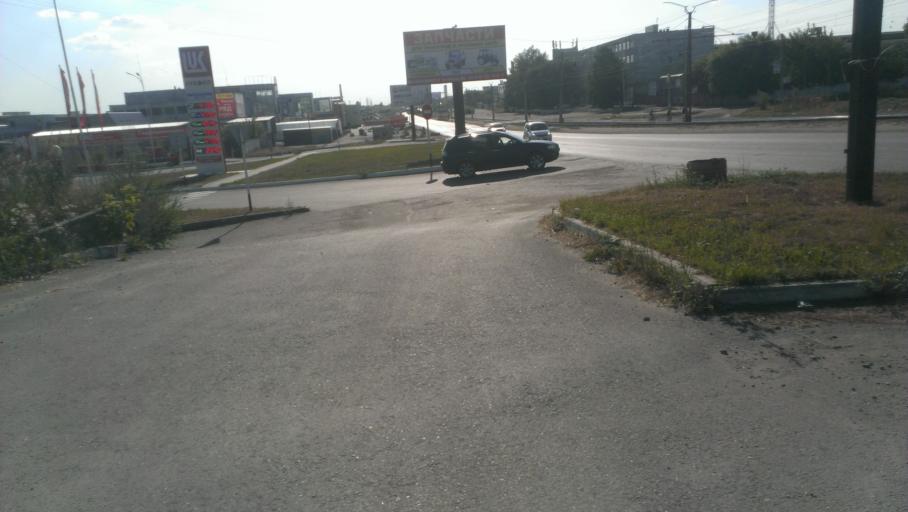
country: RU
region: Altai Krai
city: Novosilikatnyy
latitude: 53.3241
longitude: 83.6455
